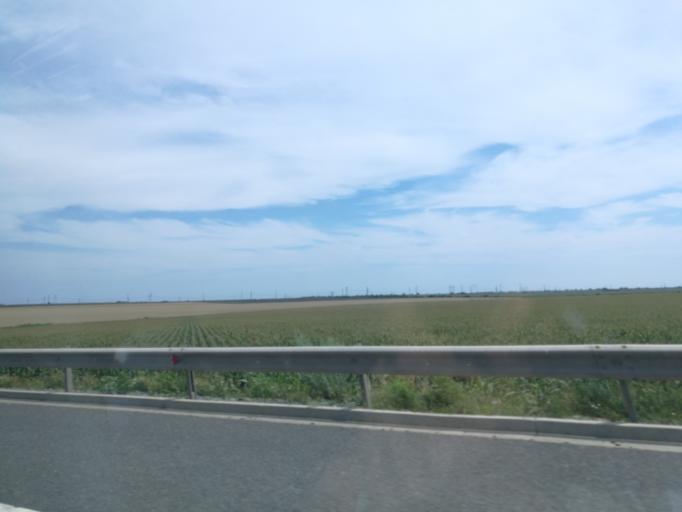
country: RO
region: Constanta
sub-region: Municipiul Constanta
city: Palazu Mare
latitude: 44.1986
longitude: 28.5524
